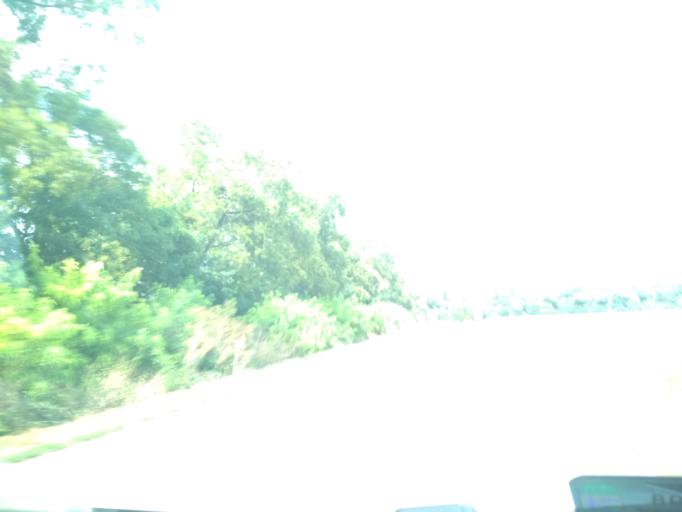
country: HU
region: Jasz-Nagykun-Szolnok
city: Tiszaszolos
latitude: 47.5175
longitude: 20.6577
